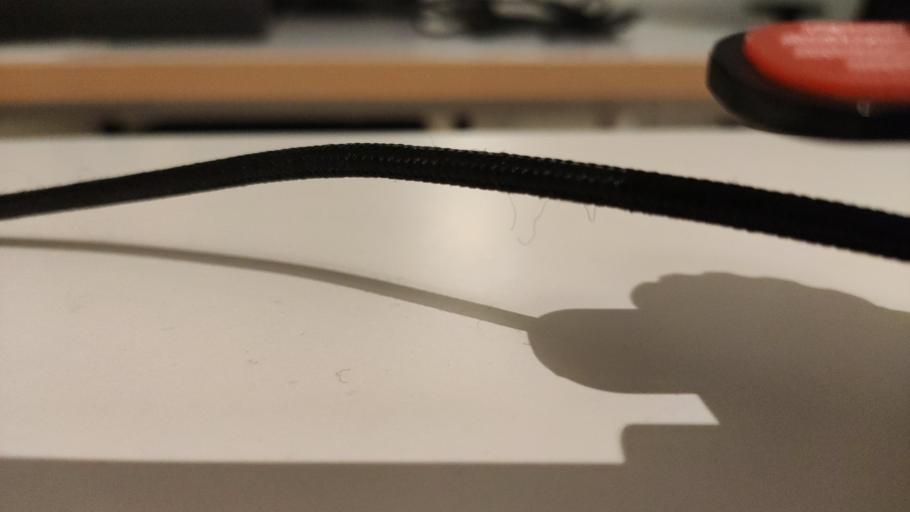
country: RU
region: Moskovskaya
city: Novosin'kovo
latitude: 56.3721
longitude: 37.3433
